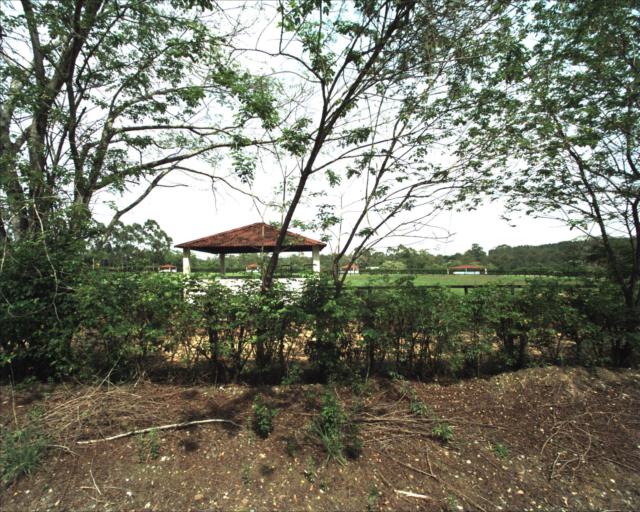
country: BR
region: Sao Paulo
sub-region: Aracoiaba Da Serra
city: Aracoiaba da Serra
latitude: -23.5594
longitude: -47.5366
